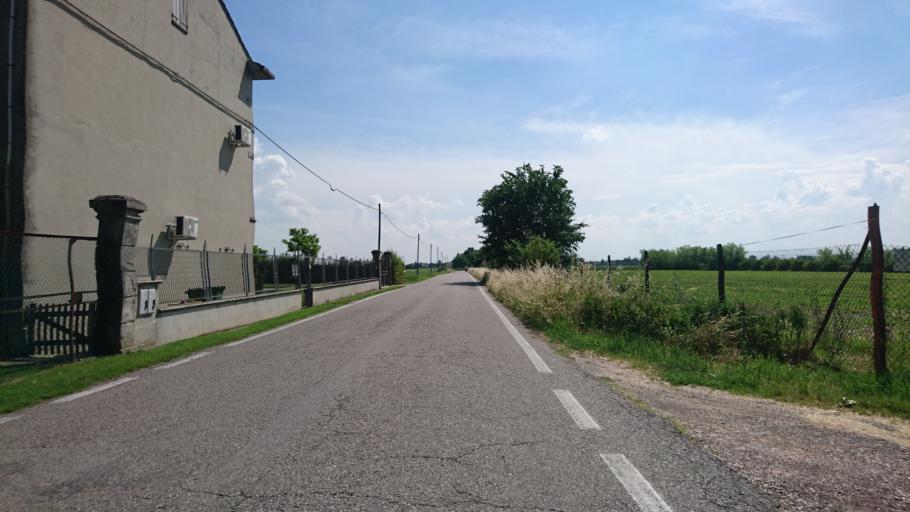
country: IT
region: Veneto
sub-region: Provincia di Rovigo
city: Castelmassa
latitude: 45.0686
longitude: 11.3354
